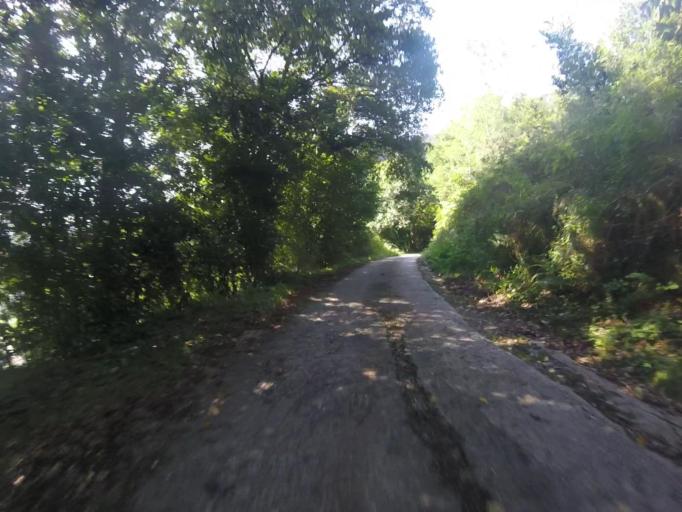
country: ES
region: Basque Country
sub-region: Provincia de Guipuzcoa
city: Irun
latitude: 43.3220
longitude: -1.7443
